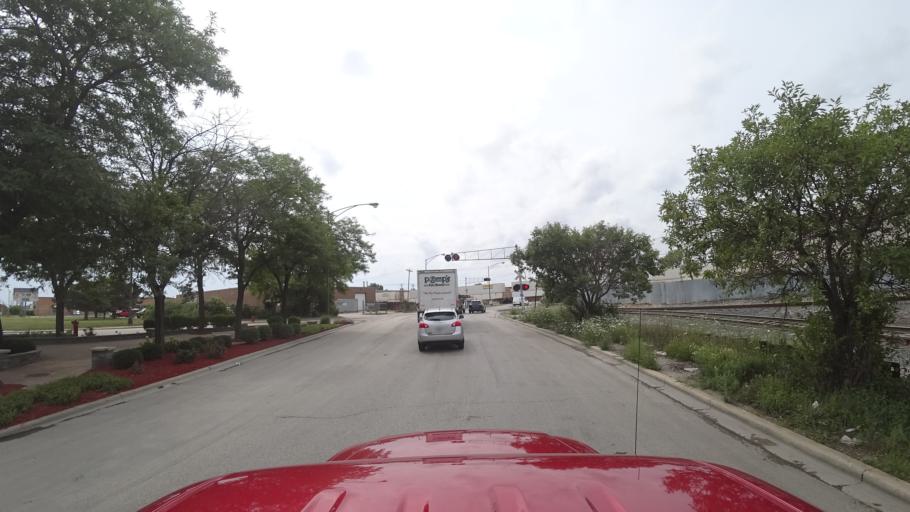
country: US
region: Illinois
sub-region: Cook County
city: Chicago
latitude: 41.8232
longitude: -87.6559
